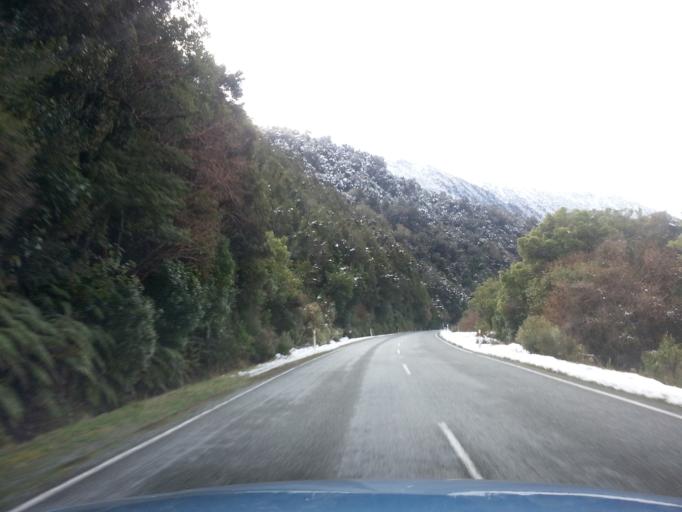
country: NZ
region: West Coast
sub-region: Grey District
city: Greymouth
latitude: -42.8114
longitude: 171.5658
